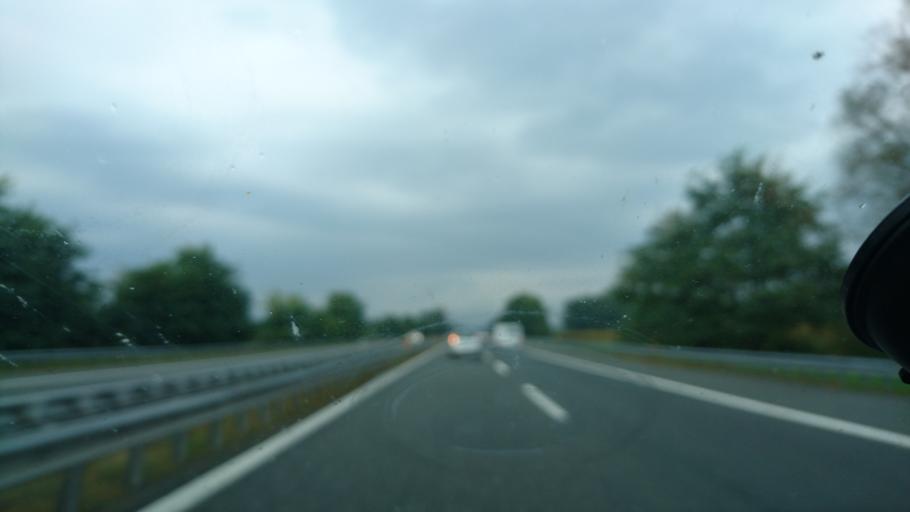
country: IT
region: Piedmont
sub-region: Provincia di Novara
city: Ghemme
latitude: 45.5828
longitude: 8.4057
